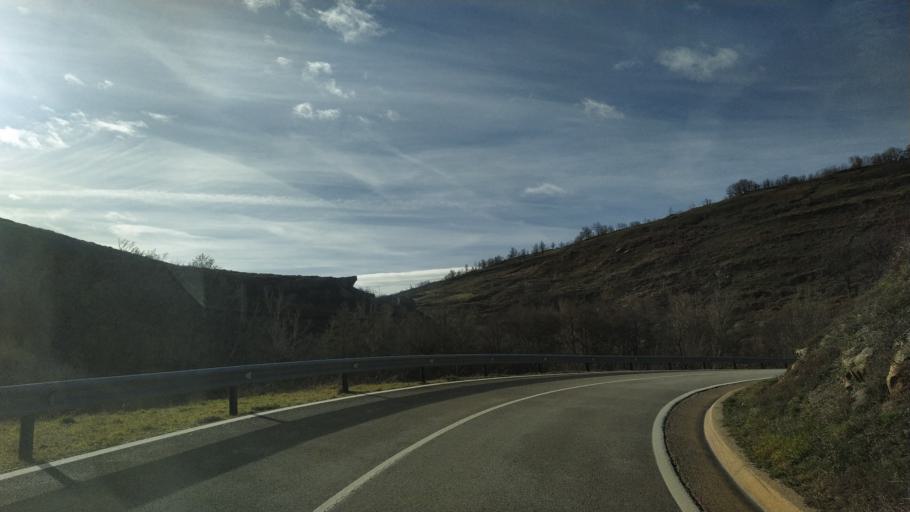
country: ES
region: Cantabria
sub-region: Provincia de Cantabria
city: San Martin de Elines
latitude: 42.8446
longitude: -3.9101
